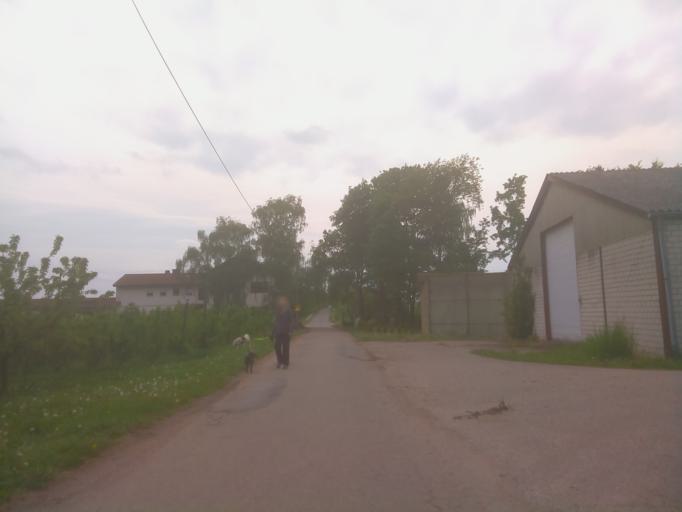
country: DE
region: Baden-Wuerttemberg
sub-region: Karlsruhe Region
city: Schriesheim
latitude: 49.4762
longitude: 8.6458
